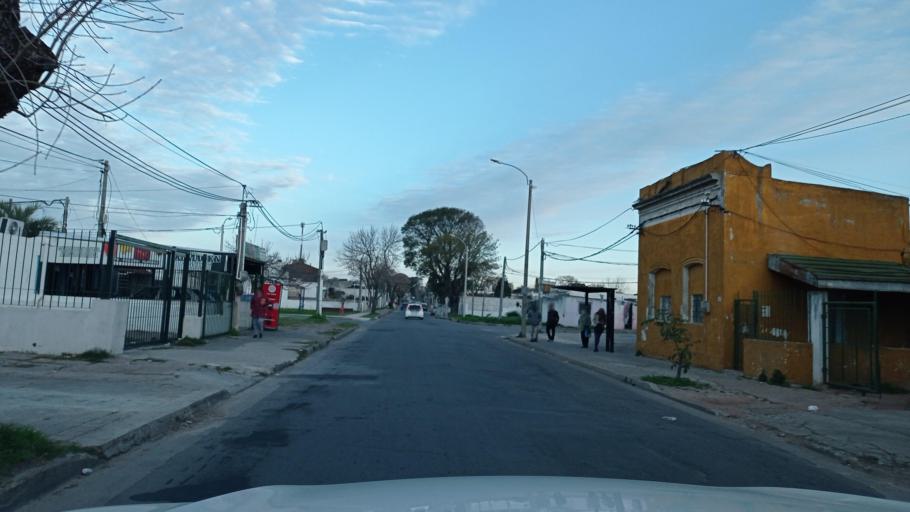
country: UY
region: Montevideo
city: Montevideo
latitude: -34.8677
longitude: -56.1468
